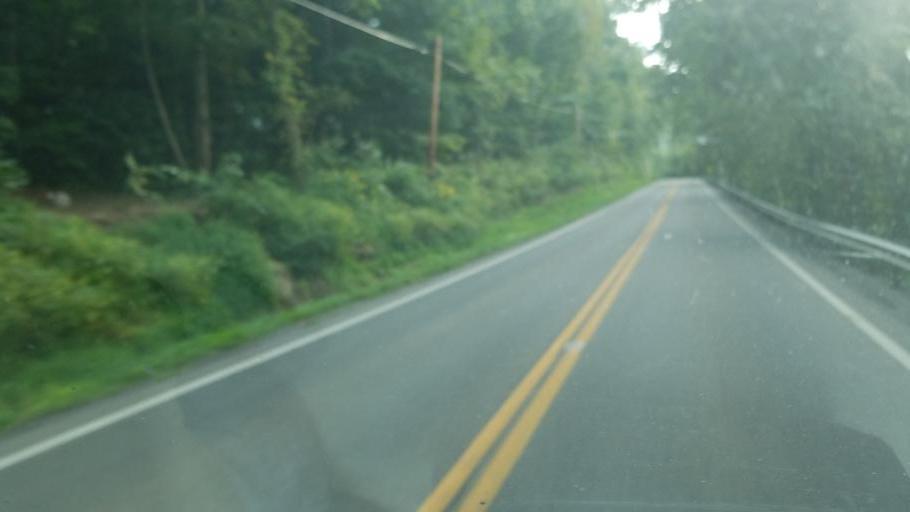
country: US
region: Ohio
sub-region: Holmes County
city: Millersburg
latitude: 40.4997
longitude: -81.9471
